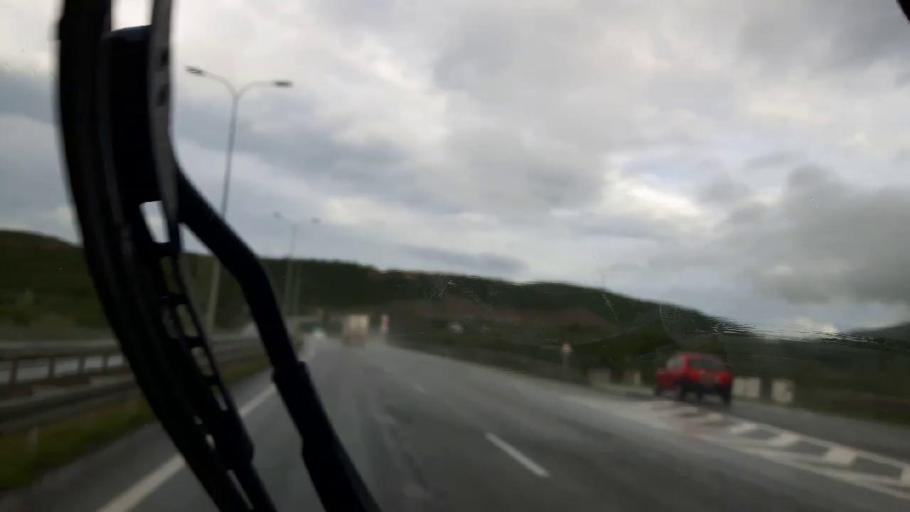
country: GE
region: Shida Kartli
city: Kaspi
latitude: 41.9947
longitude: 44.4151
